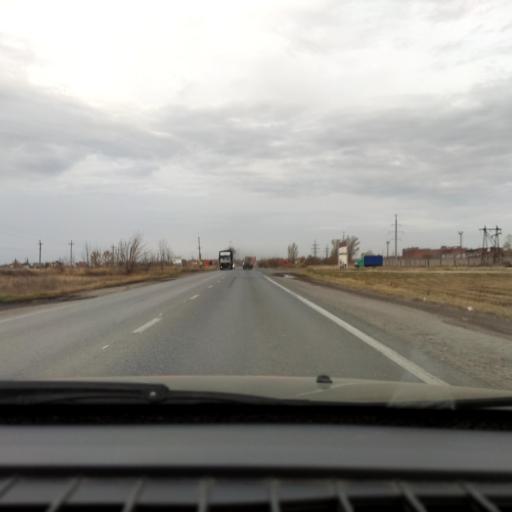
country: RU
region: Samara
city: Tol'yatti
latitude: 53.5689
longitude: 49.3459
